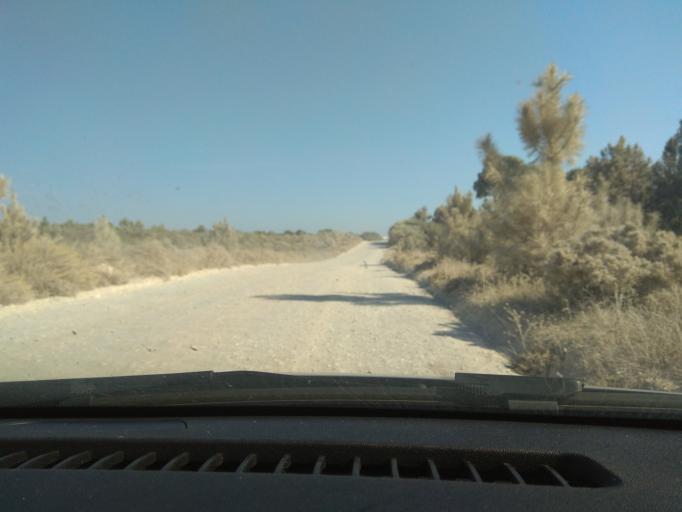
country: PT
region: Beja
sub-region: Odemira
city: Vila Nova de Milfontes
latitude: 37.7714
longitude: -8.7884
